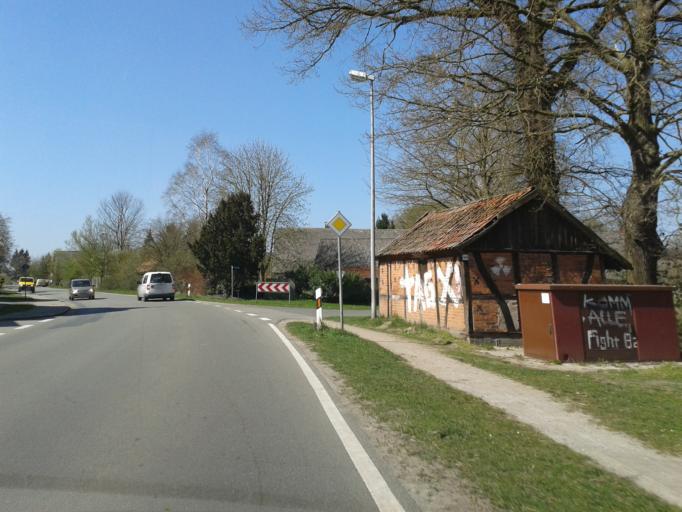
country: DE
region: Lower Saxony
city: Wustrow
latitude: 52.9394
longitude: 11.0985
